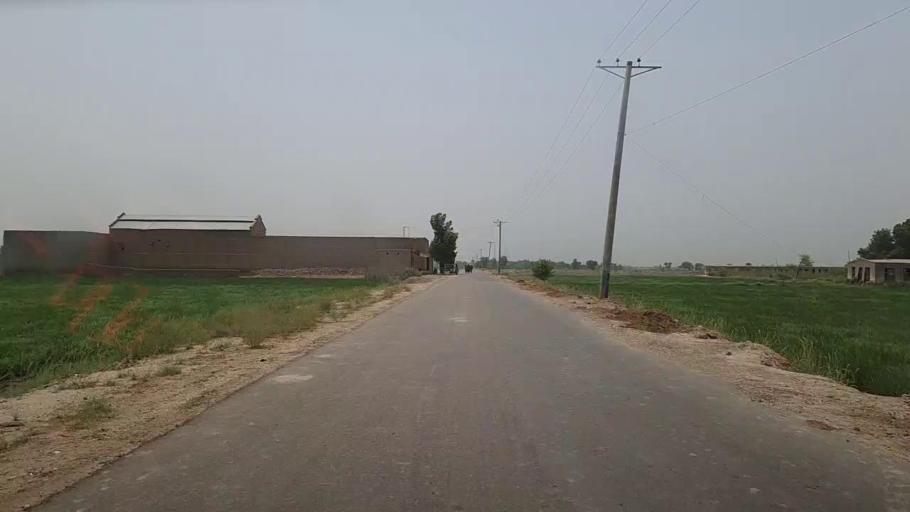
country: PK
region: Sindh
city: Sita Road
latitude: 27.0535
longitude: 67.9025
